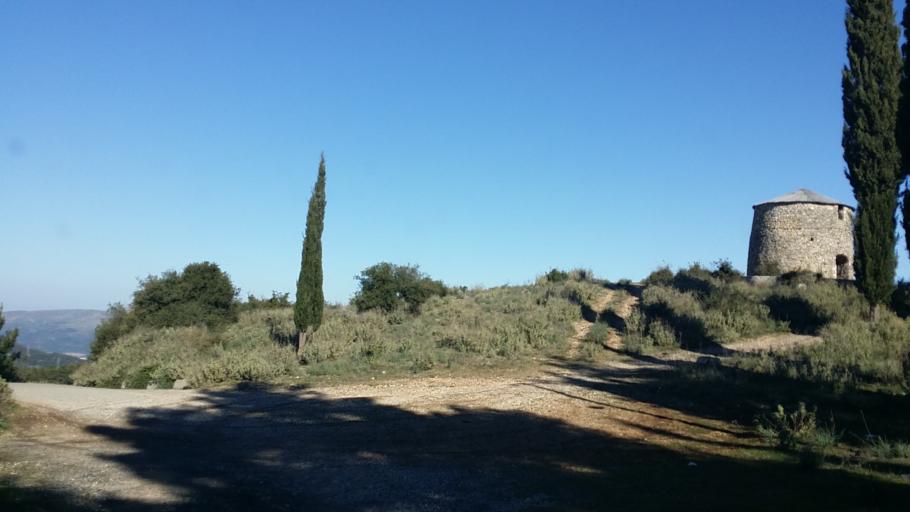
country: GR
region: West Greece
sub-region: Nomos Aitolias kai Akarnanias
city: Fitiai
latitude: 38.7002
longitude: 21.1843
